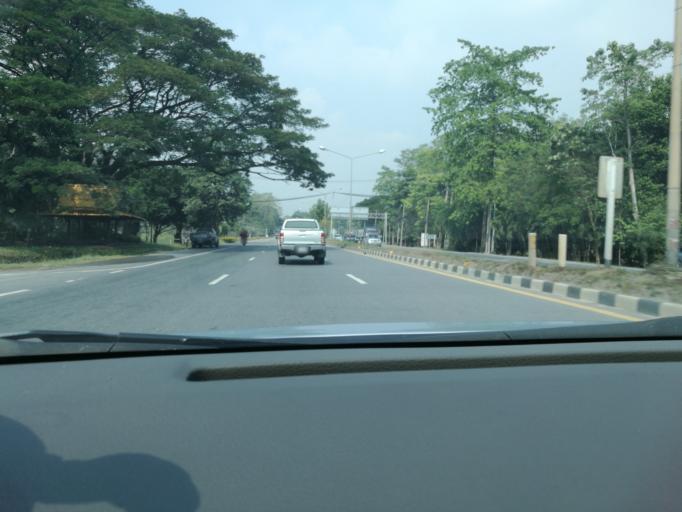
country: TH
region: Sara Buri
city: Chaloem Phra Kiat
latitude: 14.6705
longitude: 100.8864
